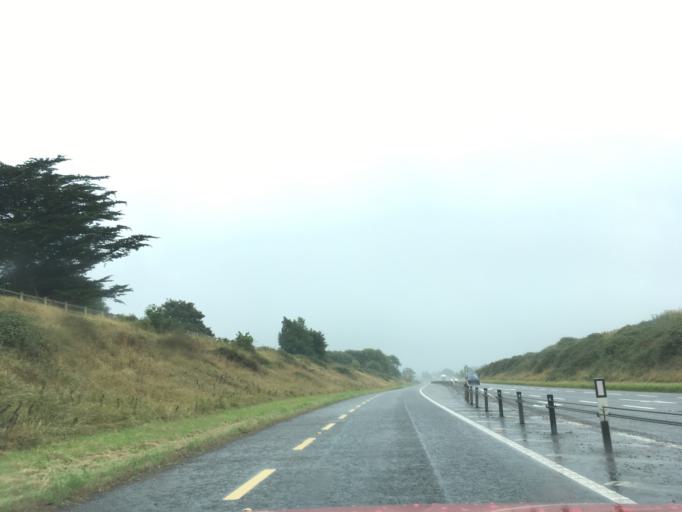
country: IE
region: Leinster
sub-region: Kilkenny
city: Piltown
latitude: 52.3534
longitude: -7.3412
